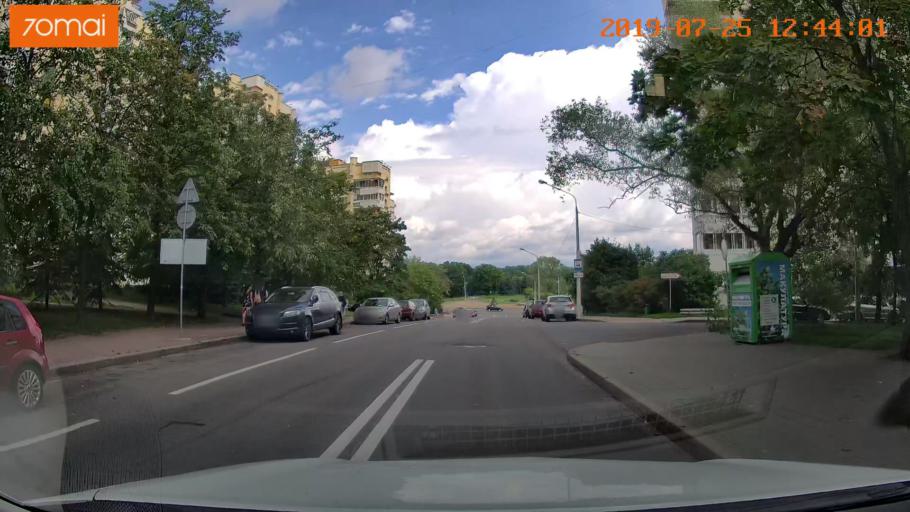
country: BY
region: Minsk
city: Minsk
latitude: 53.9161
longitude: 27.5334
